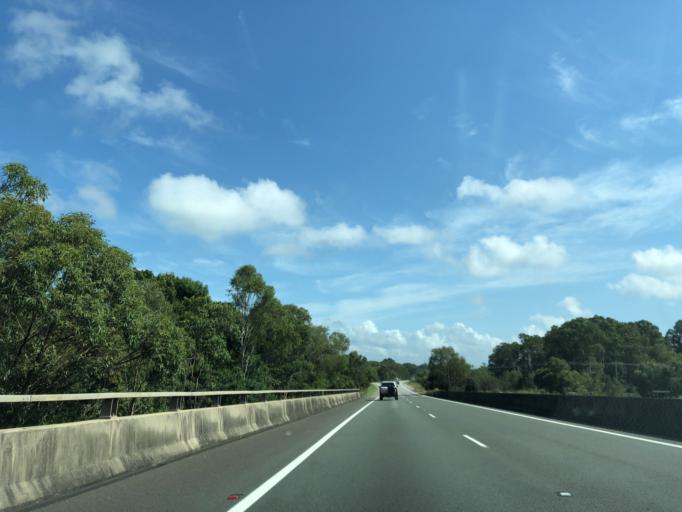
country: AU
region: New South Wales
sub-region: Byron Shire
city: Brunswick Heads
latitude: -28.6020
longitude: 153.5454
